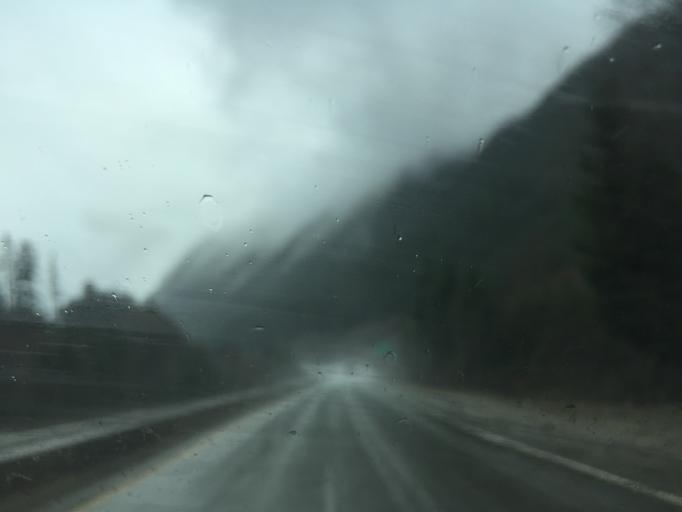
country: CA
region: British Columbia
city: Hope
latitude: 49.5264
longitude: -121.2060
